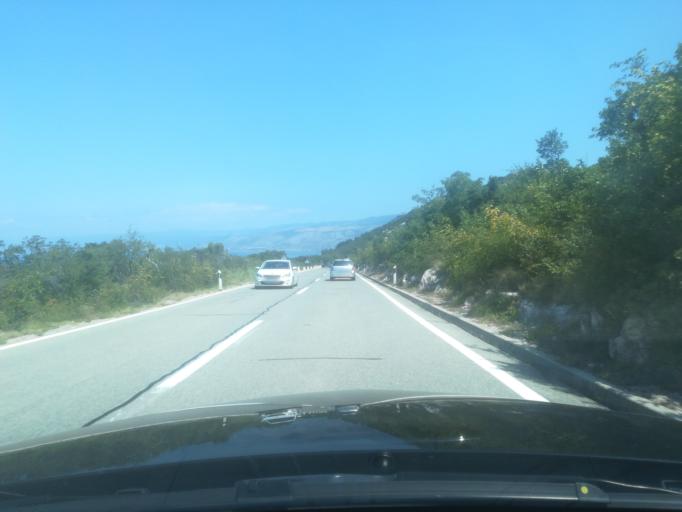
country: HR
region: Licko-Senjska
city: Senj
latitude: 44.8816
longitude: 14.9113
